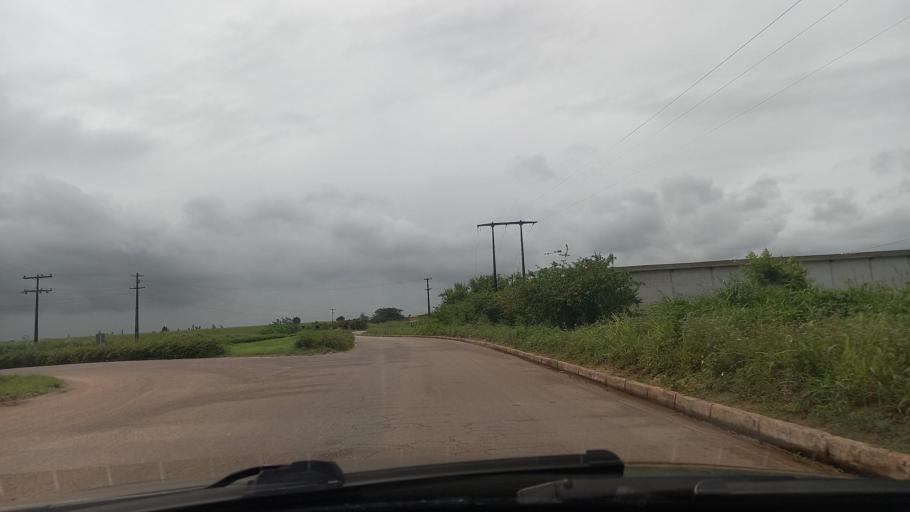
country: BR
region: Alagoas
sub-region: Sao Miguel Dos Campos
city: Sao Miguel dos Campos
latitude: -9.8070
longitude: -36.2089
